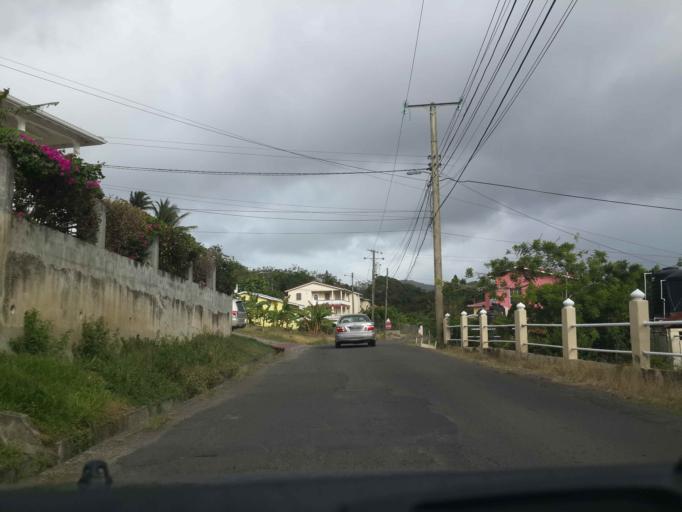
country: LC
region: Gros-Islet
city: Gros Islet
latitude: 14.0493
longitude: -60.9639
